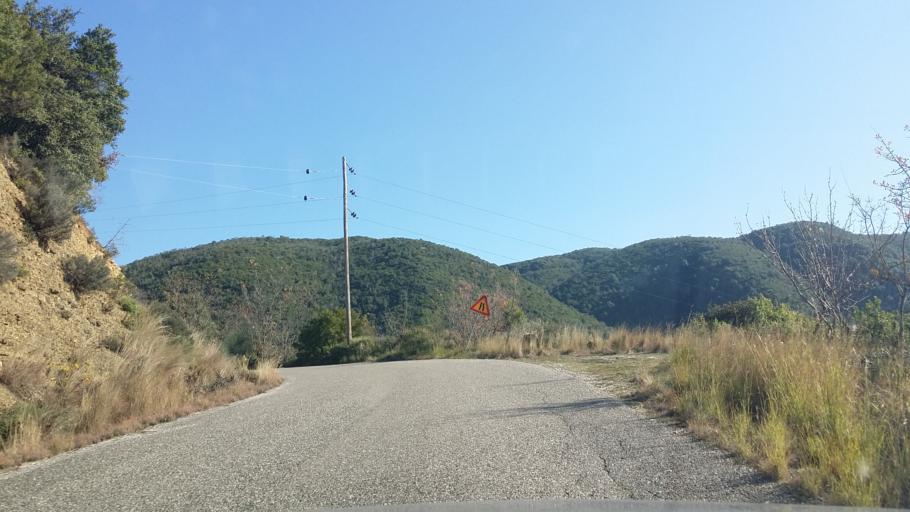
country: GR
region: West Greece
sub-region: Nomos Aitolias kai Akarnanias
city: Krikellos
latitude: 38.9885
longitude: 21.2166
